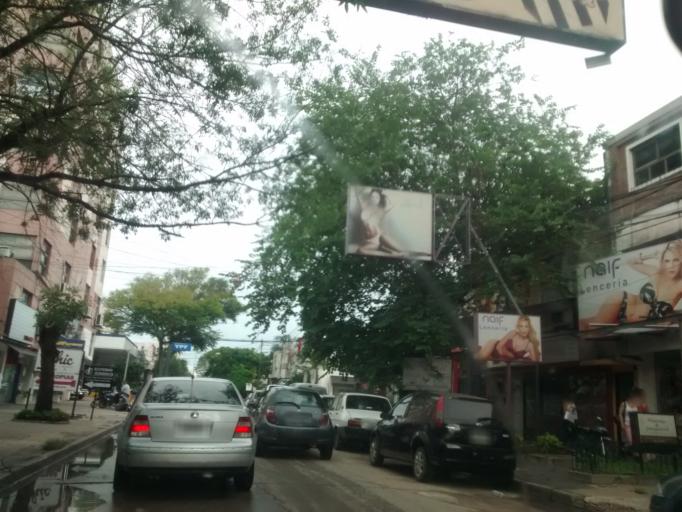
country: AR
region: Chaco
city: Resistencia
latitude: -27.4500
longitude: -58.9835
